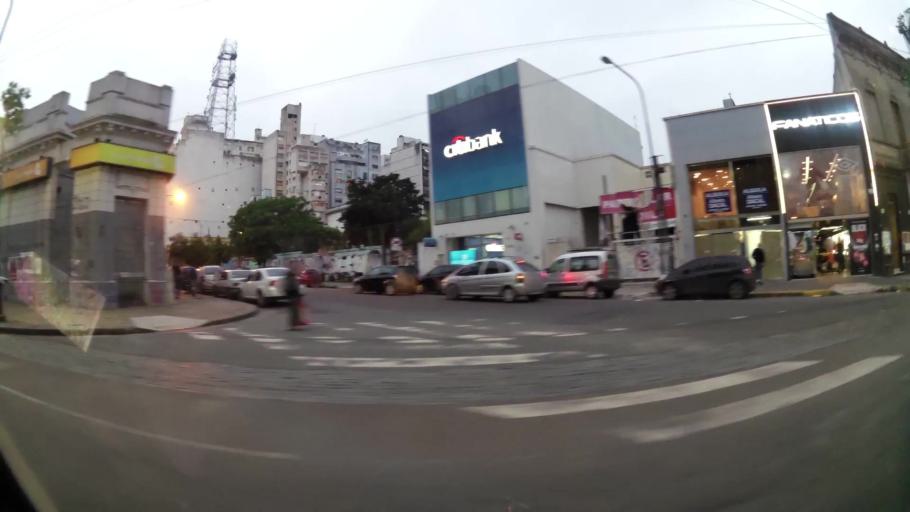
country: AR
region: Buenos Aires
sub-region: Partido de La Plata
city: La Plata
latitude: -34.9155
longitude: -57.9550
